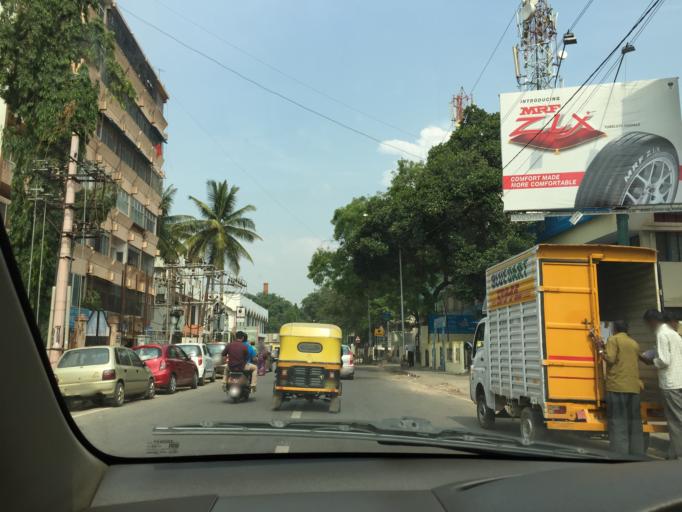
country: IN
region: Karnataka
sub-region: Bangalore Urban
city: Bangalore
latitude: 12.9797
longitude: 77.6058
